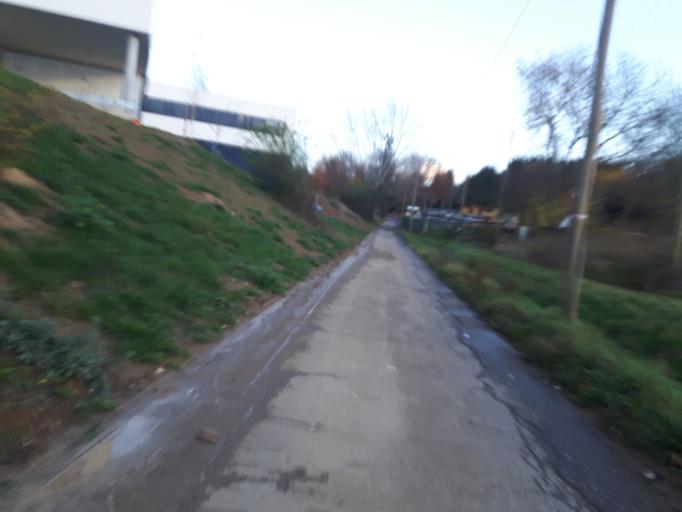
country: DE
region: Baden-Wuerttemberg
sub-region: Regierungsbezirk Stuttgart
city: Flein
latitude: 49.1184
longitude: 9.2168
